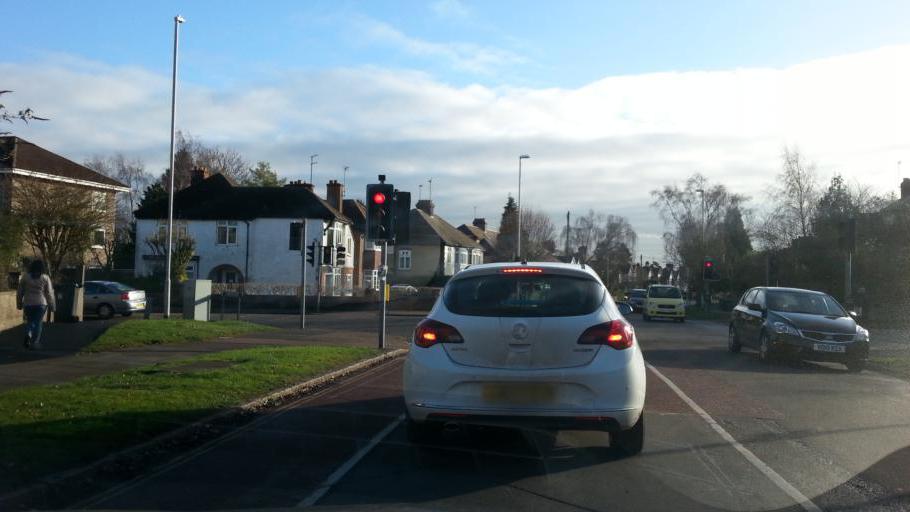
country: GB
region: England
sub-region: Cambridgeshire
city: Cambridge
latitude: 52.2211
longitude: 0.1183
